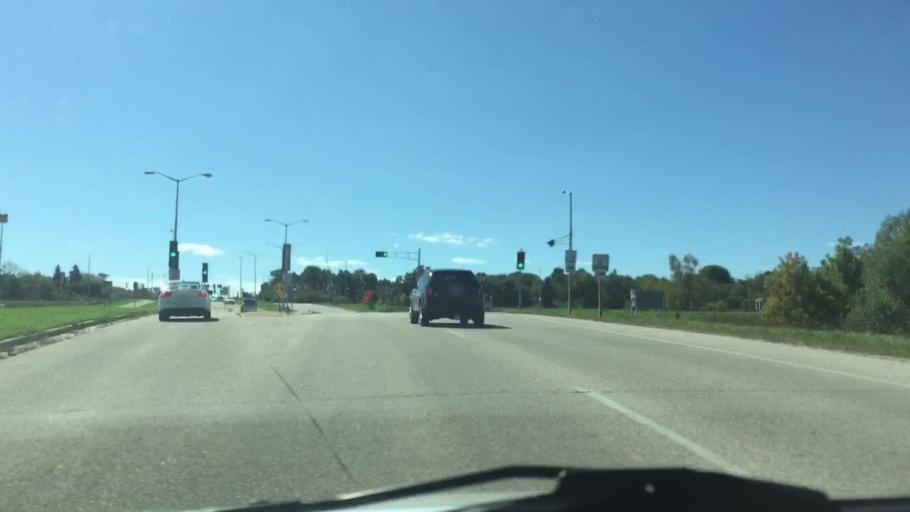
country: US
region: Wisconsin
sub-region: Waukesha County
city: Pewaukee
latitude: 43.0522
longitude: -88.2855
